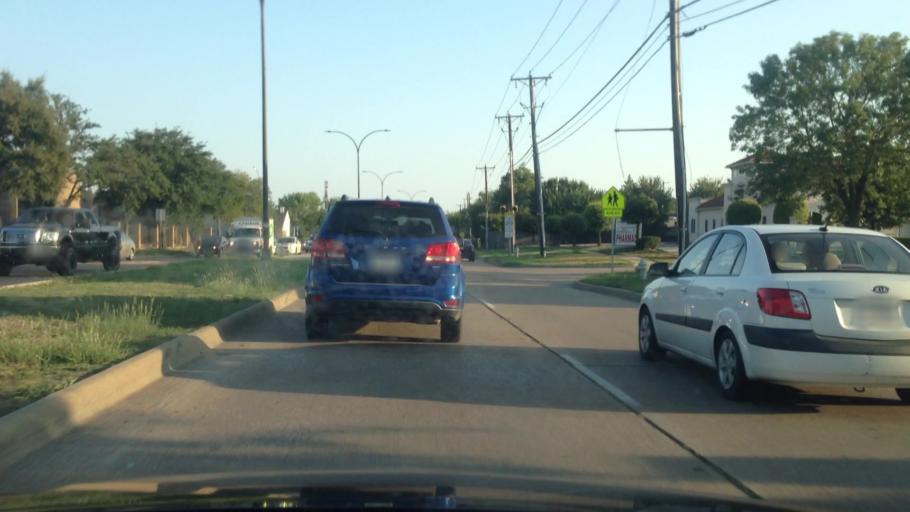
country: US
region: Texas
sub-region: Tarrant County
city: Dalworthington Gardens
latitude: 32.6694
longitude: -97.1150
